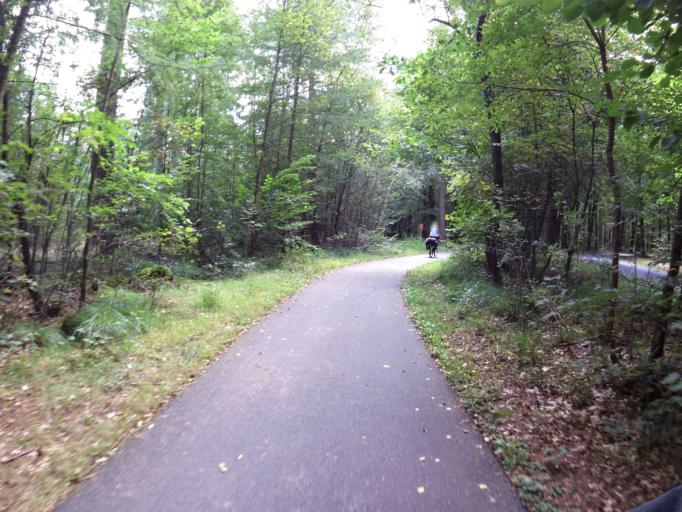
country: NL
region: Drenthe
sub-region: Gemeente Borger-Odoorn
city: Borger
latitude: 52.9585
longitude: 6.7588
